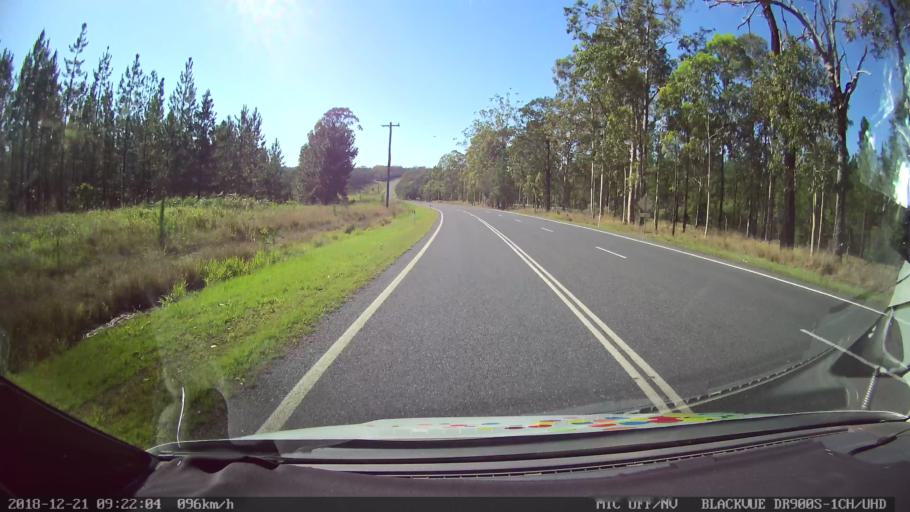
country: AU
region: New South Wales
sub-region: Clarence Valley
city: Maclean
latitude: -29.3375
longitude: 153.0019
